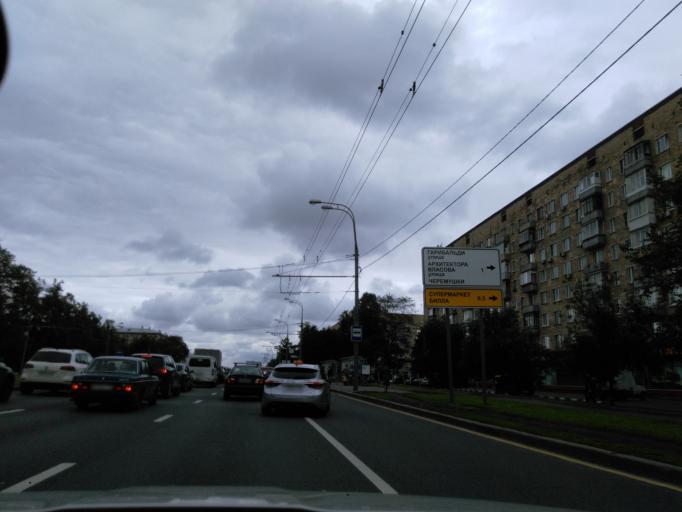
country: RU
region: Moskovskaya
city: Semenovskoye
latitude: 55.6777
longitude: 37.5303
